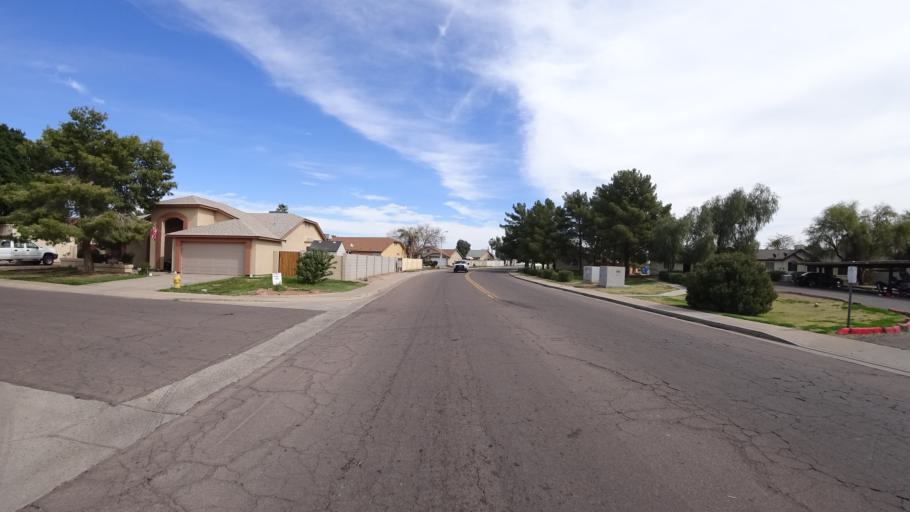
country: US
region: Arizona
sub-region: Maricopa County
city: Glendale
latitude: 33.4872
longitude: -112.2053
